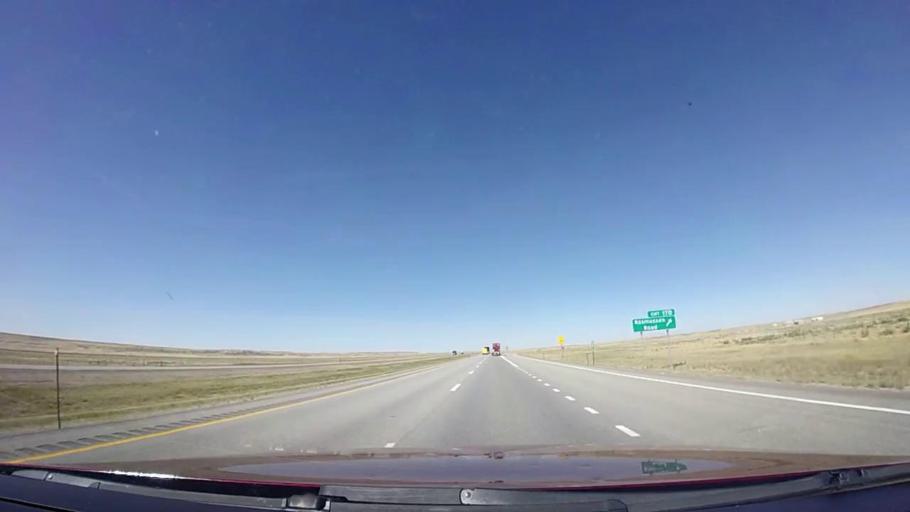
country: US
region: Wyoming
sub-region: Carbon County
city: Rawlins
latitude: 41.6664
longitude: -108.0258
